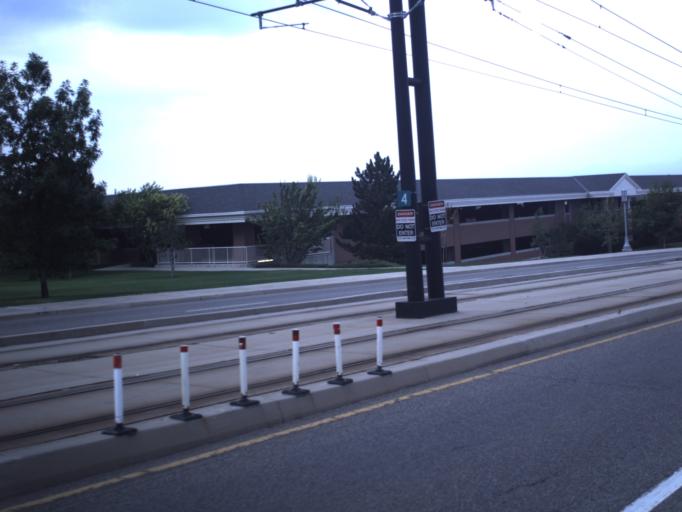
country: US
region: Utah
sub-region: Salt Lake County
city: Salt Lake City
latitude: 40.7617
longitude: -111.8371
